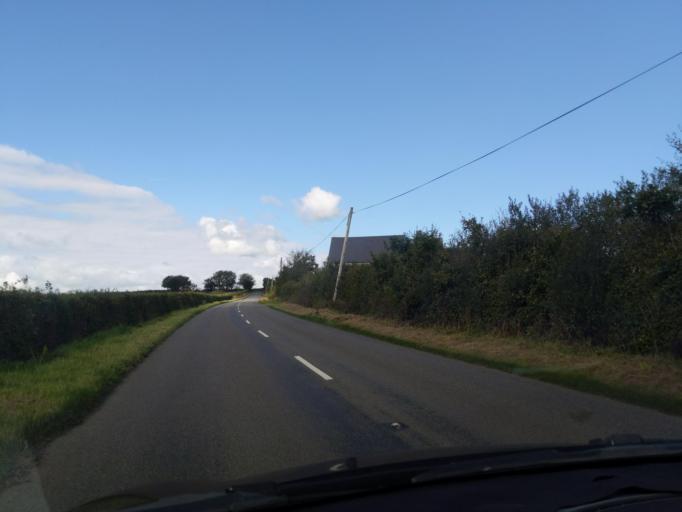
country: GB
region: England
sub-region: Cornwall
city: Werrington
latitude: 50.7021
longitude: -4.3242
